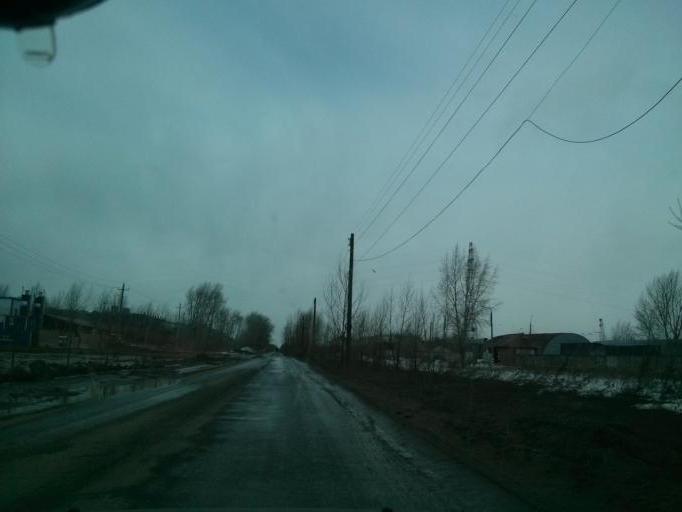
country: RU
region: Nizjnij Novgorod
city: Afonino
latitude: 56.2870
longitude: 44.1178
